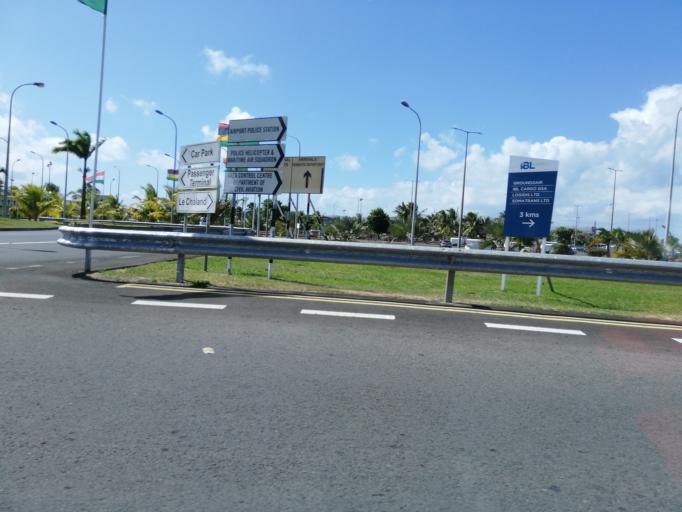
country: MU
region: Grand Port
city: Plaine Magnien
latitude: -20.4342
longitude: 57.6744
